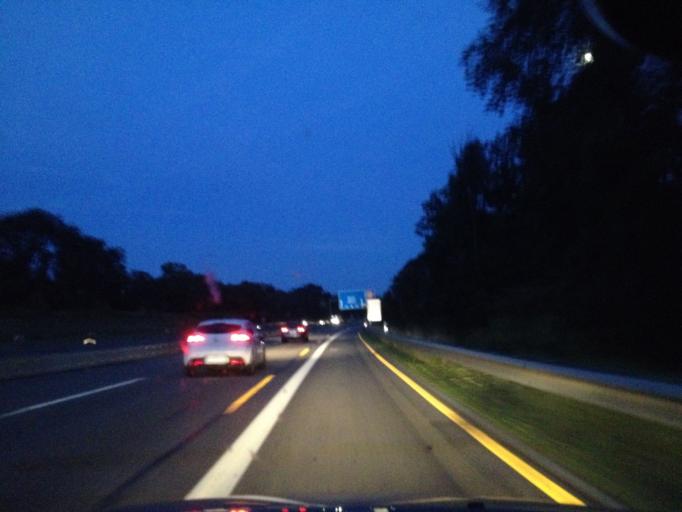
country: DE
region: Bavaria
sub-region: Swabia
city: Leipheim
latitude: 48.4528
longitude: 10.1997
